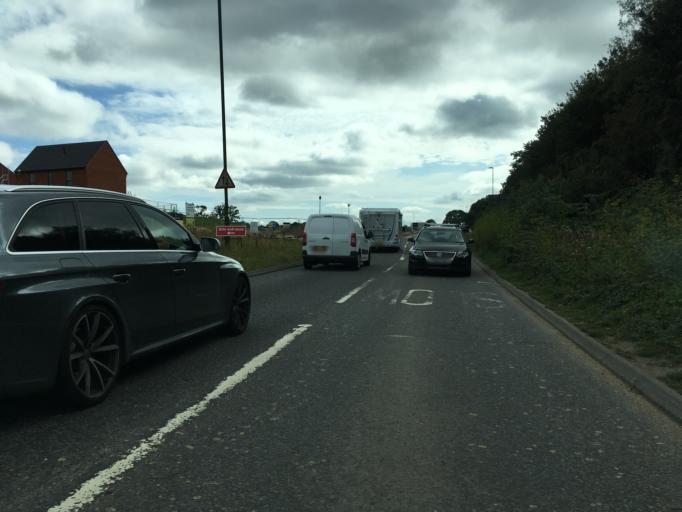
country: GB
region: England
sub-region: West Sussex
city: Broadfield
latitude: 51.0850
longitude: -0.1966
